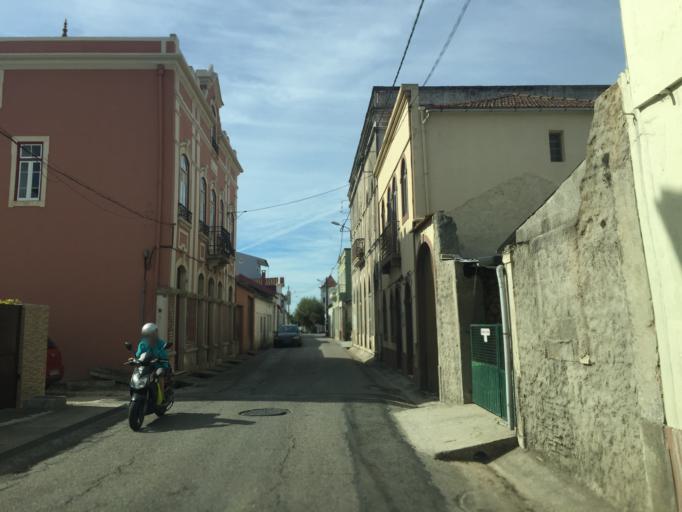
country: PT
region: Coimbra
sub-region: Figueira da Foz
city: Lavos
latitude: 40.0705
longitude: -8.8055
